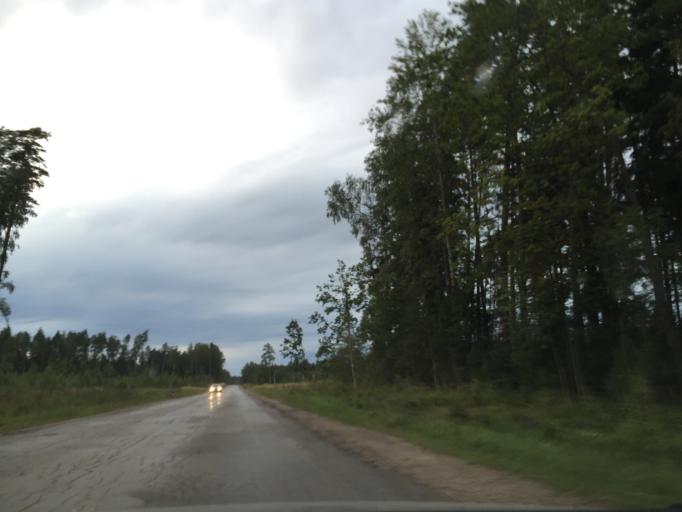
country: LV
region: Vecumnieki
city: Vecumnieki
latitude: 56.4078
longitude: 24.6372
